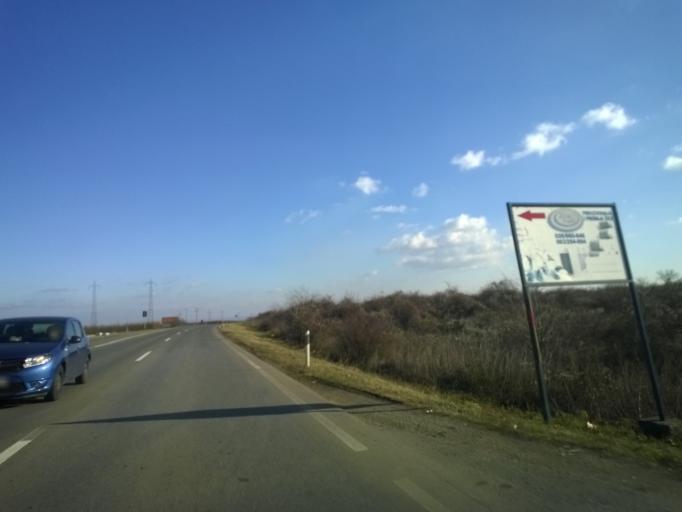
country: RS
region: Central Serbia
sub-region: Podunavski Okrug
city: Smederevo
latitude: 44.6121
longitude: 20.9212
